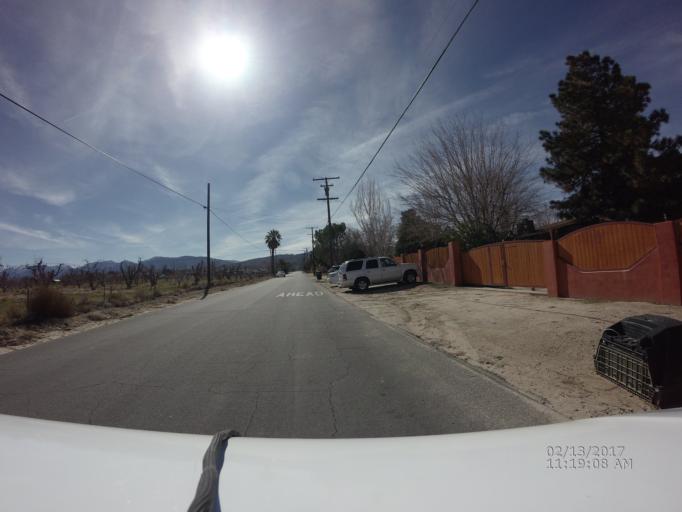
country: US
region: California
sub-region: Los Angeles County
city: Littlerock
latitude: 34.5236
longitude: -117.9925
